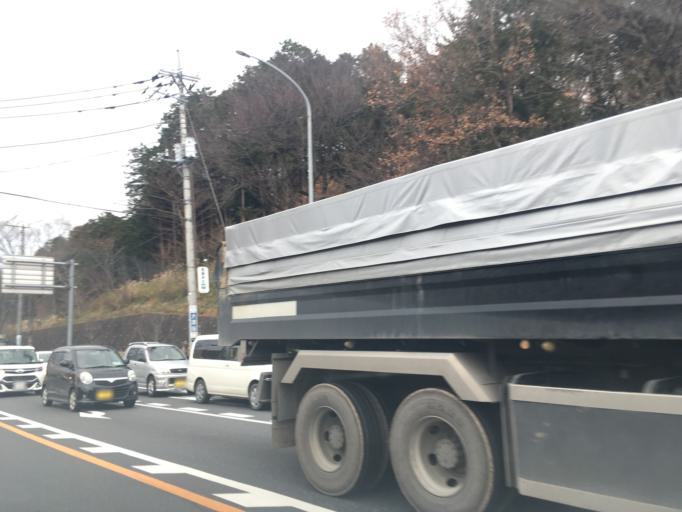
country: JP
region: Saitama
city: Hanno
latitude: 35.8650
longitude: 139.3135
